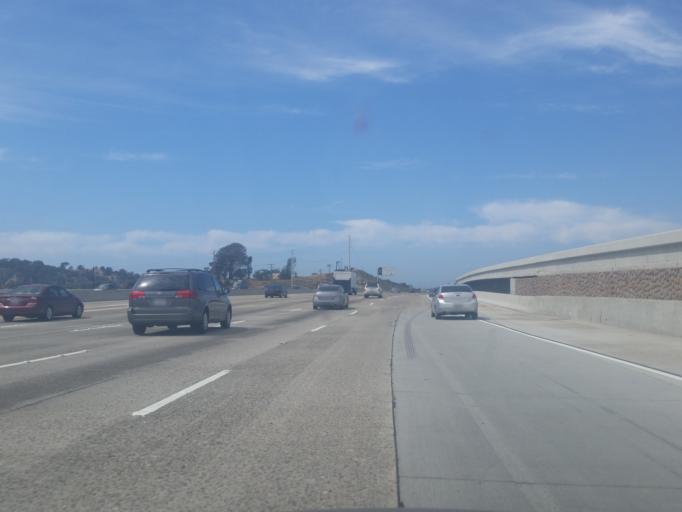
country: US
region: California
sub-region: San Diego County
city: Del Mar
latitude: 32.9175
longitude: -117.2337
